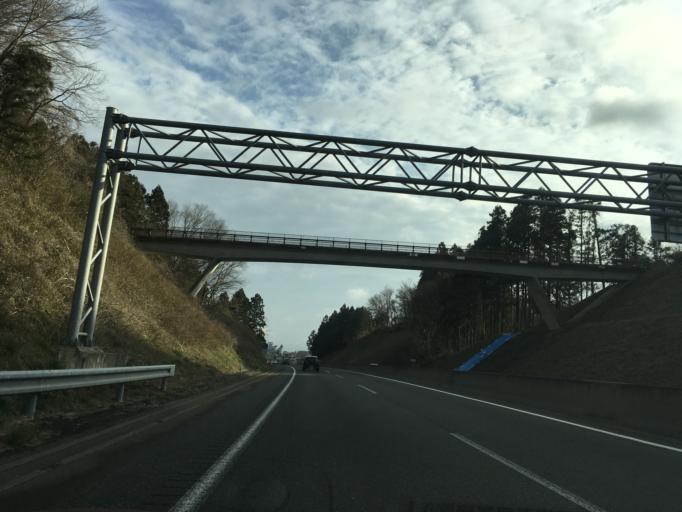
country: JP
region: Miyagi
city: Tomiya
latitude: 38.3623
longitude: 140.8822
